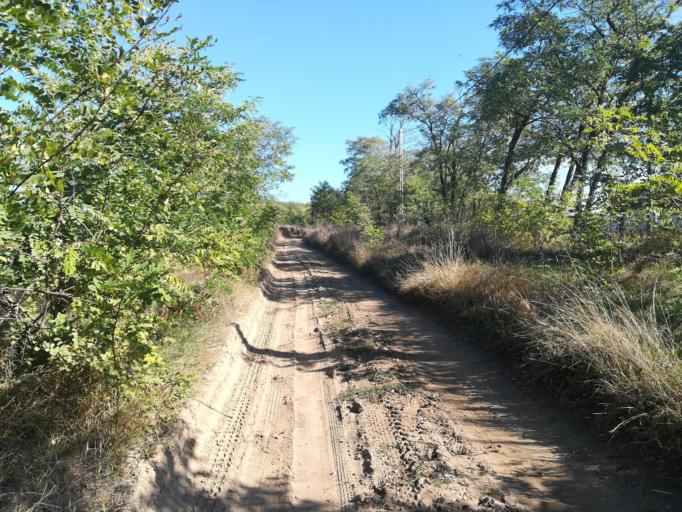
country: HU
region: Pest
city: Csomor
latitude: 47.5703
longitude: 19.1922
